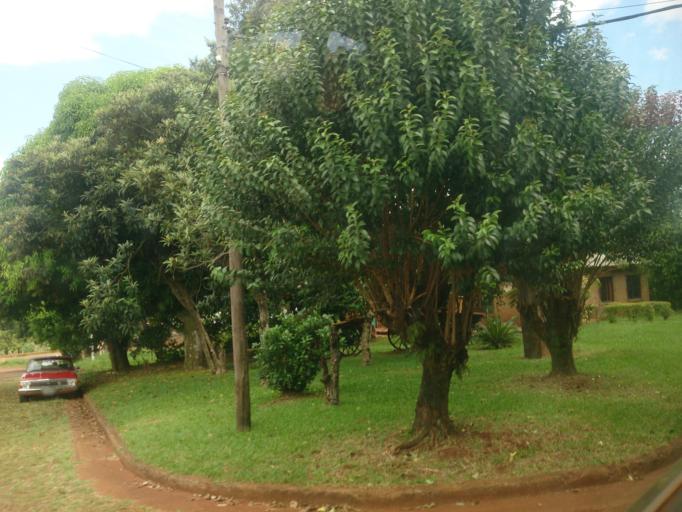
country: AR
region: Misiones
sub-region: Departamento de Obera
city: Obera
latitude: -27.4927
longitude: -55.1049
